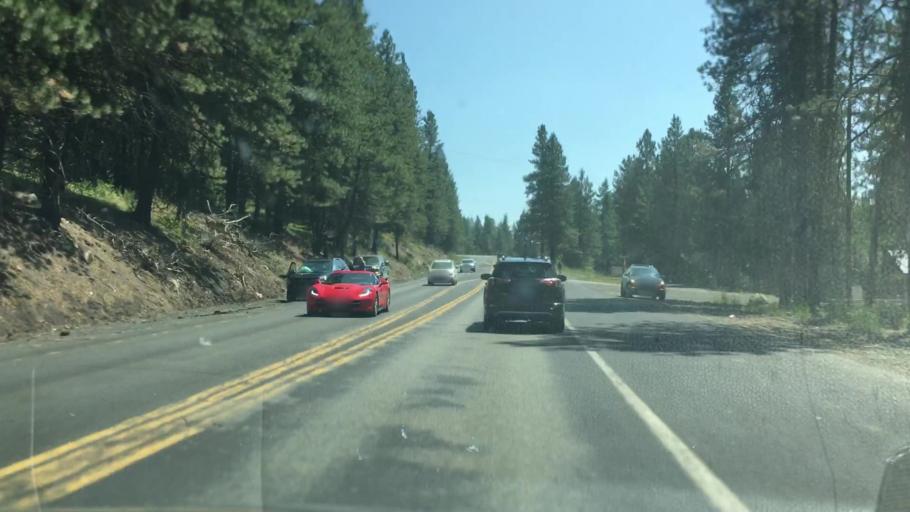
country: US
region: Idaho
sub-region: Valley County
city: McCall
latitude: 44.9347
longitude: -116.1654
